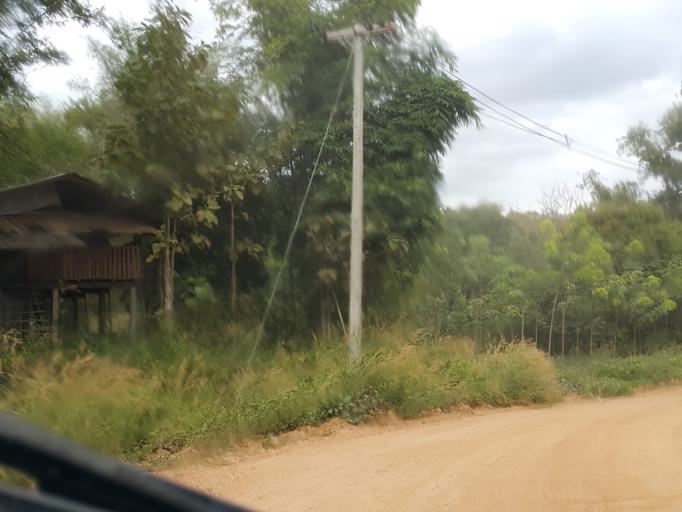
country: TH
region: Lampang
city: Chae Hom
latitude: 18.5761
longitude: 99.4458
